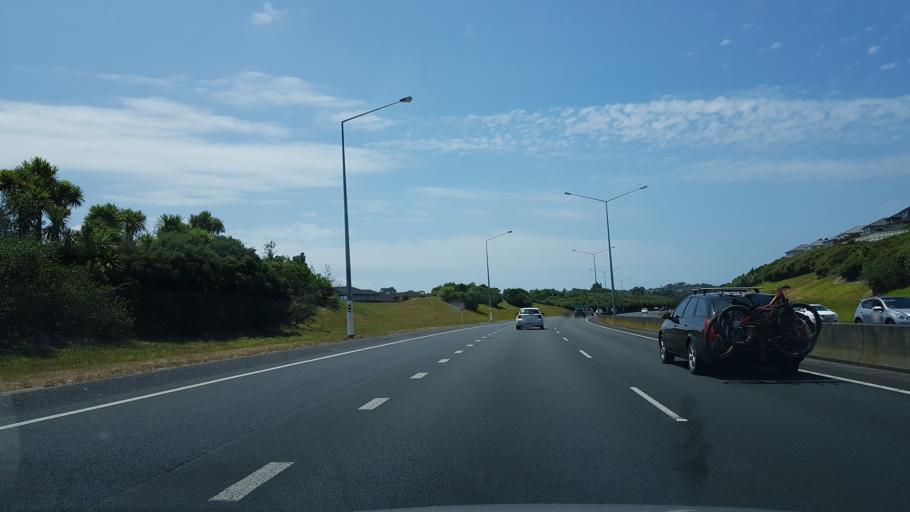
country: NZ
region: Auckland
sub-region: Auckland
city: Rothesay Bay
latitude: -36.7685
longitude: 174.6875
